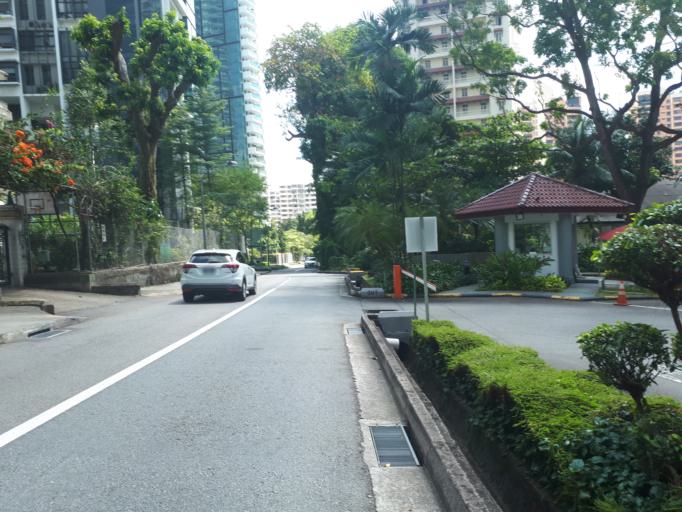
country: SG
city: Singapore
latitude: 1.2977
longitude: 103.8355
